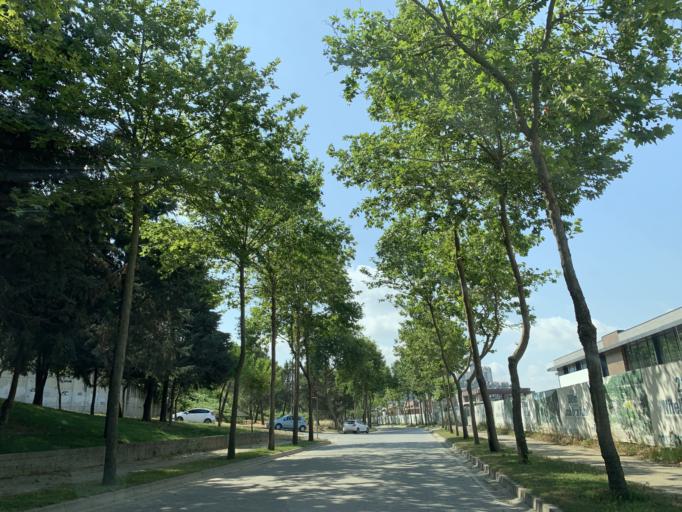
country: TR
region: Istanbul
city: Esenyurt
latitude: 41.0638
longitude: 28.6965
